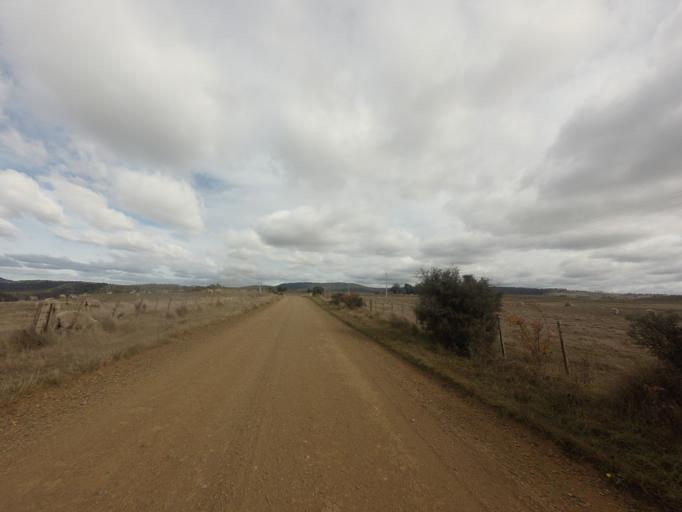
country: AU
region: Tasmania
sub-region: Brighton
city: Bridgewater
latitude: -42.4242
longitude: 147.3904
